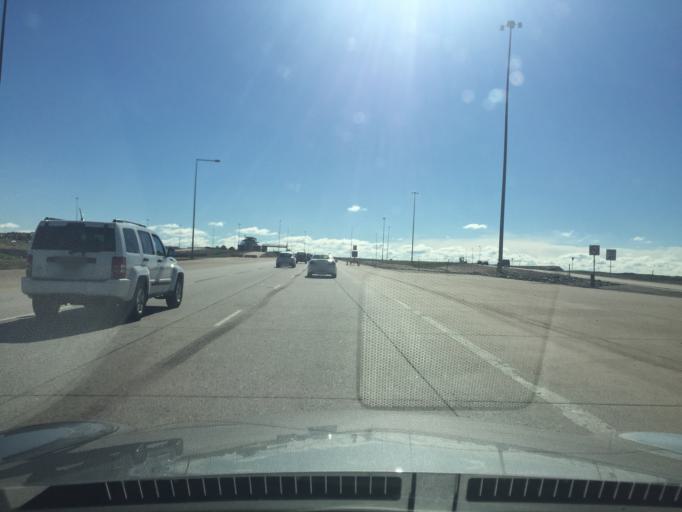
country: US
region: Colorado
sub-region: Adams County
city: Aurora
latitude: 39.8332
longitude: -104.7276
